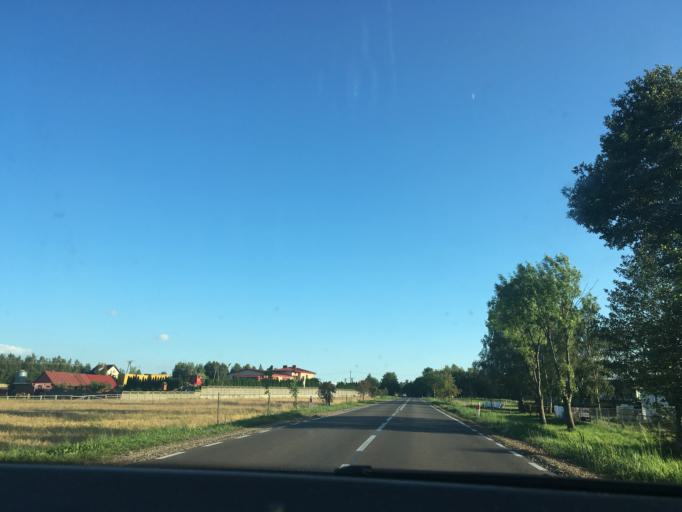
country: PL
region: Masovian Voivodeship
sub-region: Powiat losicki
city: Losice
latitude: 52.2024
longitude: 22.7282
